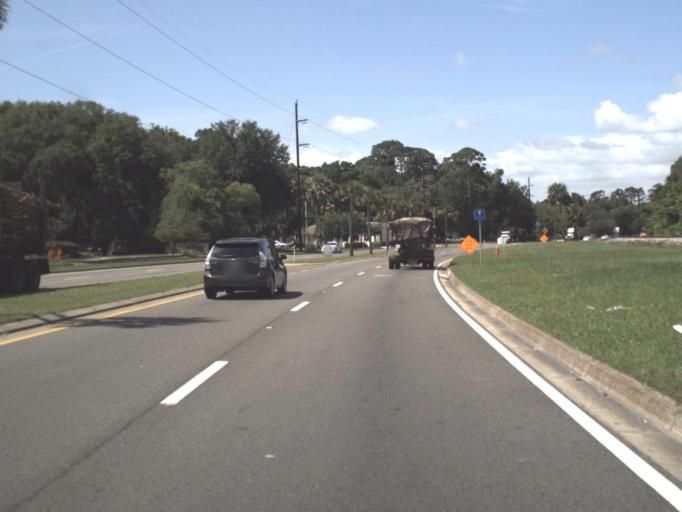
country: US
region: Florida
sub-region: Nassau County
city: Fernandina Beach
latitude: 30.6361
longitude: -81.4591
